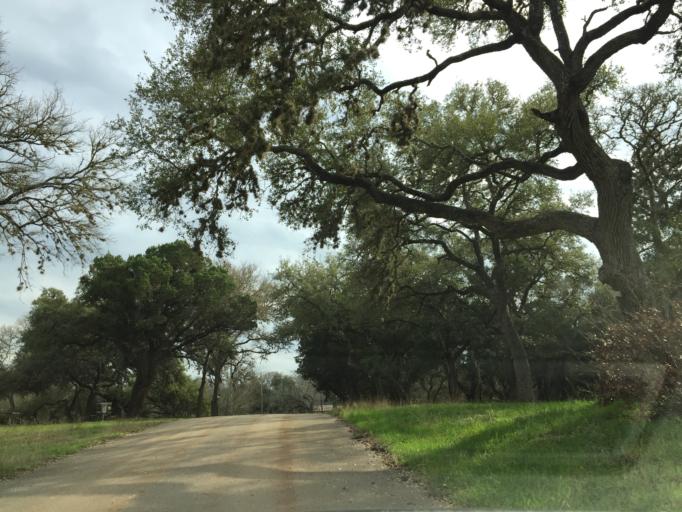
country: US
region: Texas
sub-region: Hays County
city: Dripping Springs
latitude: 30.1299
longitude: -98.0137
